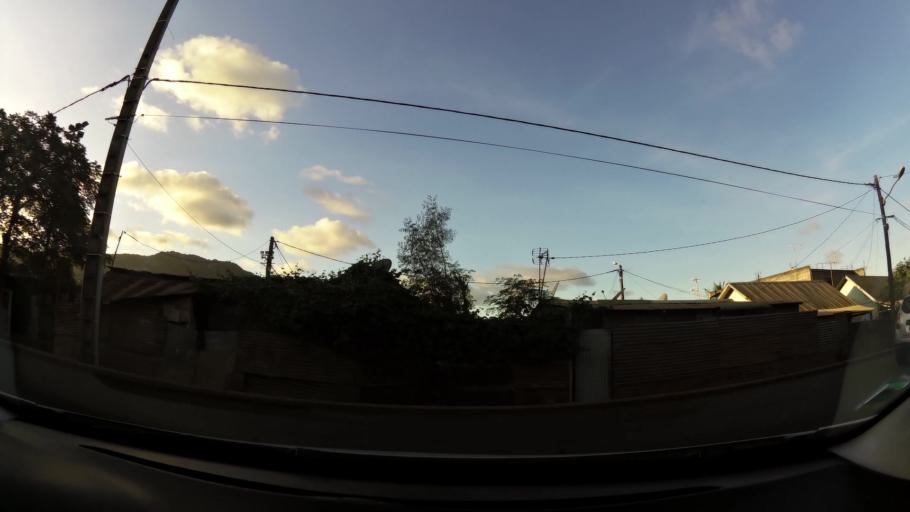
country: YT
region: Dembeni
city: Dembeni
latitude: -12.8436
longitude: 45.1854
